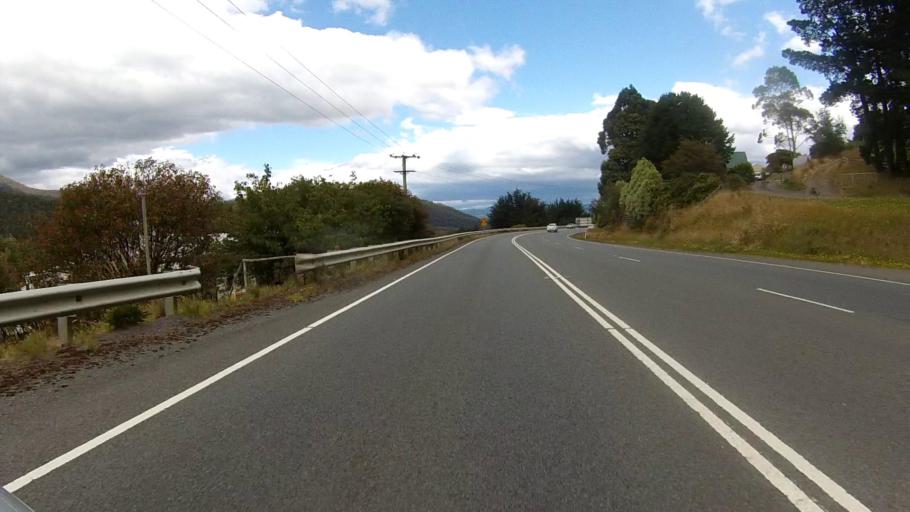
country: AU
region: Tasmania
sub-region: Huon Valley
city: Huonville
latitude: -42.9769
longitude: 147.1433
